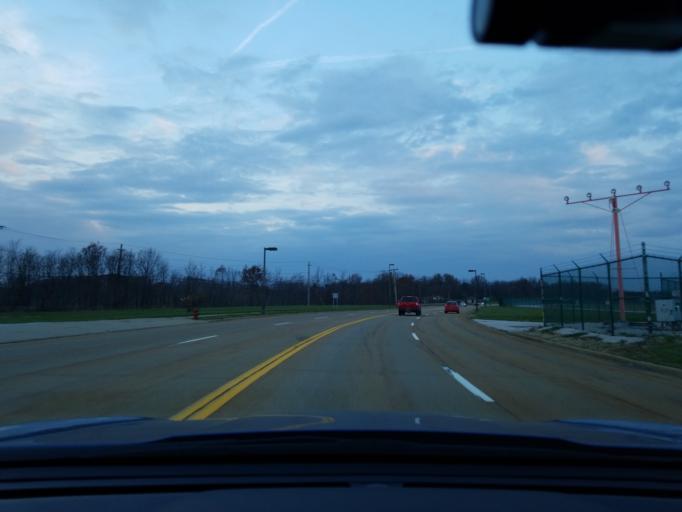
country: US
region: Ohio
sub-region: Cuyahoga County
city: Olmsted Falls
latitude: 41.3959
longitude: -81.8793
